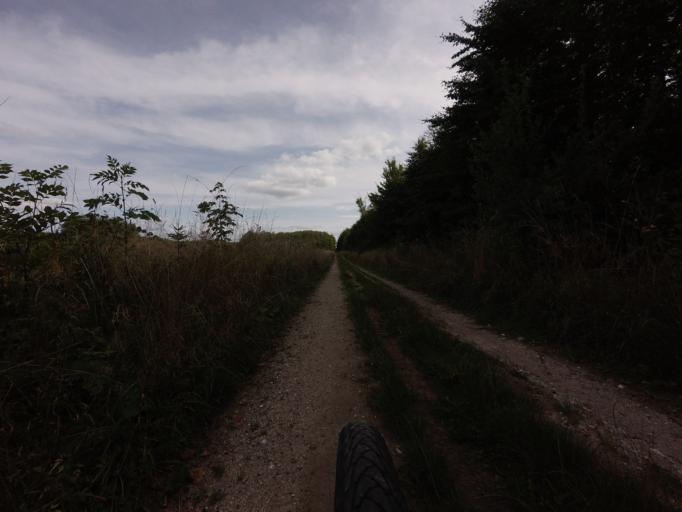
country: DK
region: Zealand
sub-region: Faxe Kommune
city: Fakse Ladeplads
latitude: 55.2311
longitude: 12.1854
